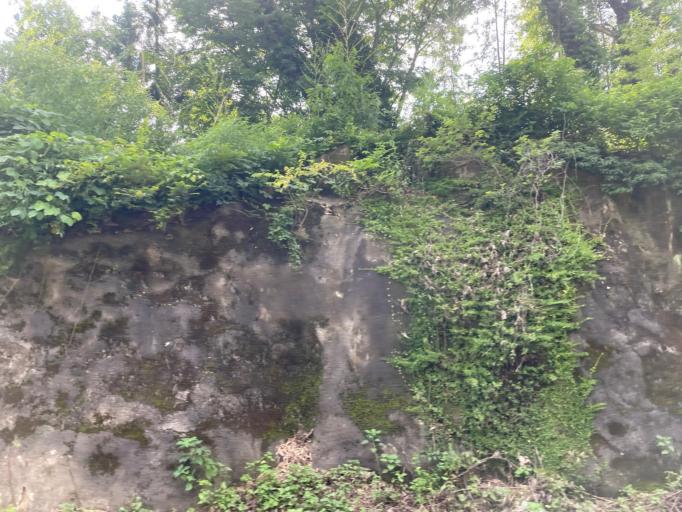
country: JP
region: Gunma
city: Numata
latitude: 36.7391
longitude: 138.9852
